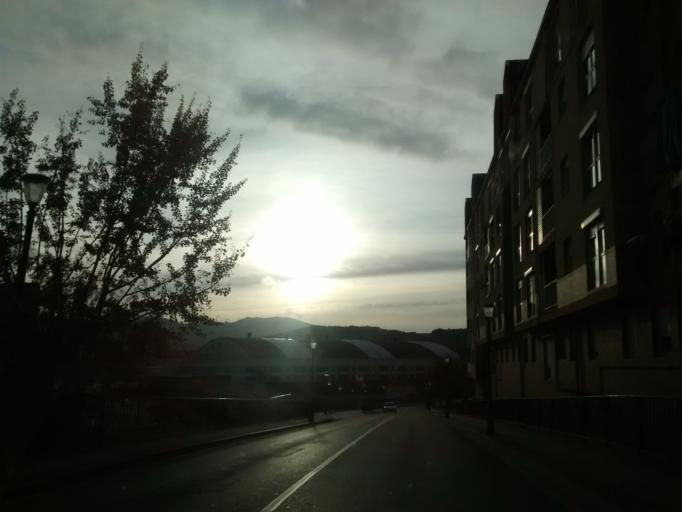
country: ES
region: Cantabria
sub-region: Provincia de Cantabria
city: Torrelavega
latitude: 43.3445
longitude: -4.0466
